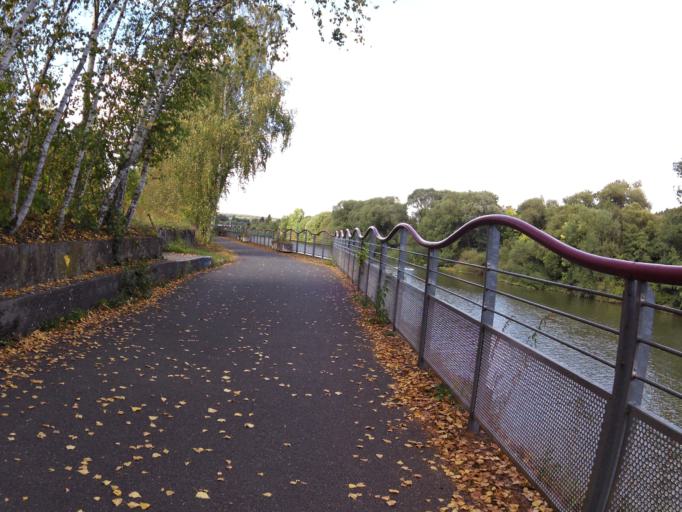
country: DE
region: Saarland
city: Kleinblittersdorf
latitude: 49.1495
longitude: 7.0379
